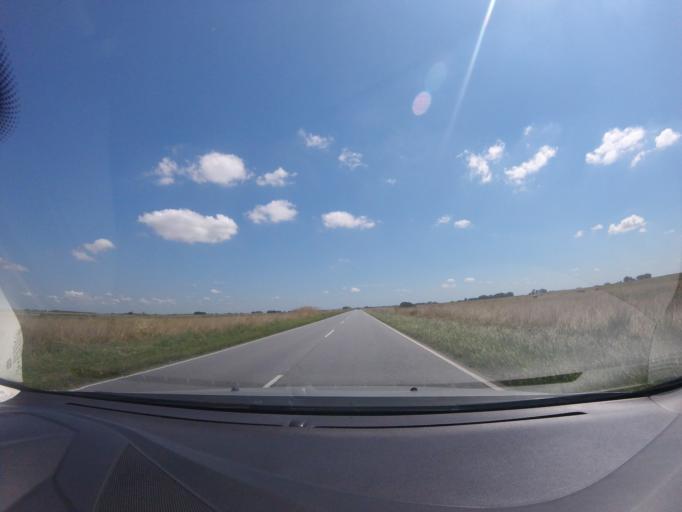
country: AR
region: Buenos Aires
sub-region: Partido de Rauch
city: Rauch
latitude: -37.0137
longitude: -59.0031
